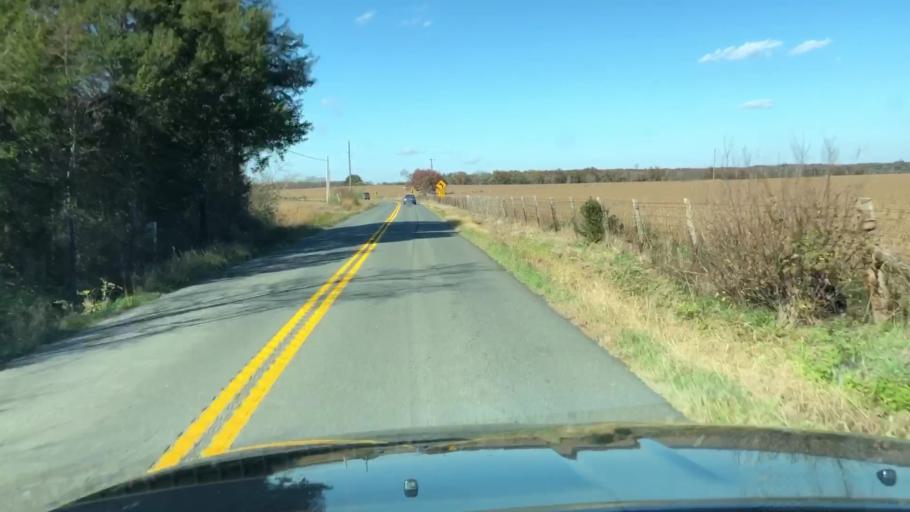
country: US
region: Virginia
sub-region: Fauquier County
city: Bealeton
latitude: 38.5101
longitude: -77.7782
